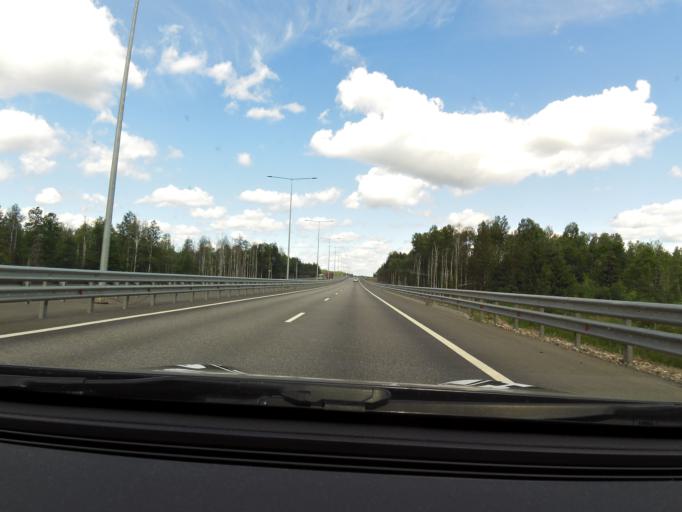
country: RU
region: Tverskaya
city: Krasnomayskiy
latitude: 57.6254
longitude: 34.2413
